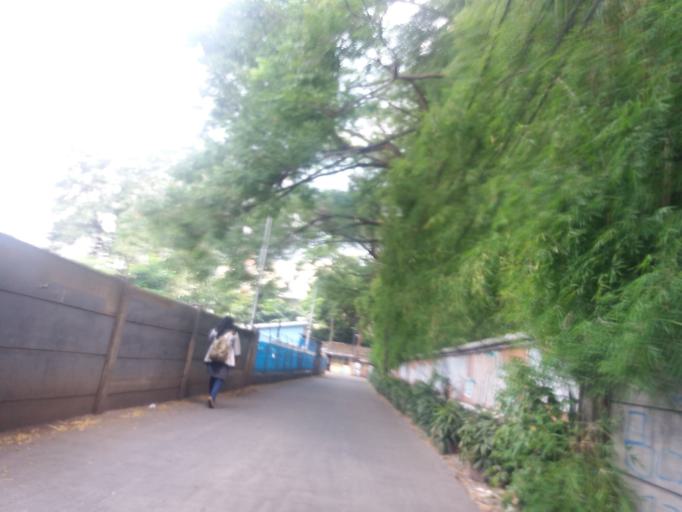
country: ID
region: Jakarta Raya
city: Jakarta
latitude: -6.2224
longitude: 106.8234
